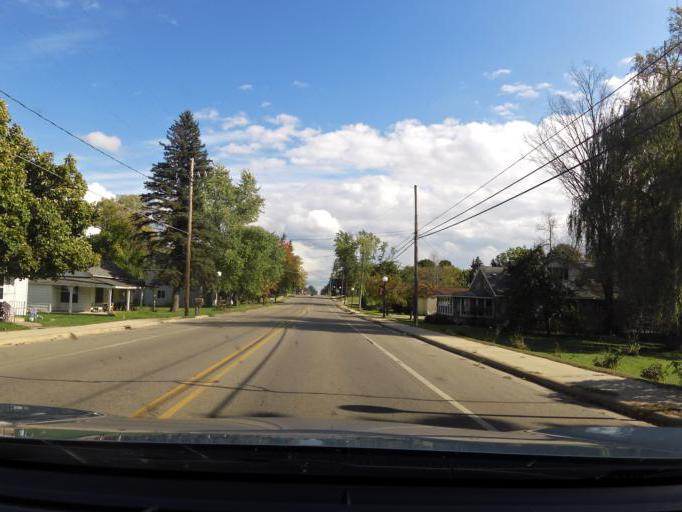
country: US
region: Michigan
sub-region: Roscommon County
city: Roscommon
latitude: 44.4975
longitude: -84.5907
